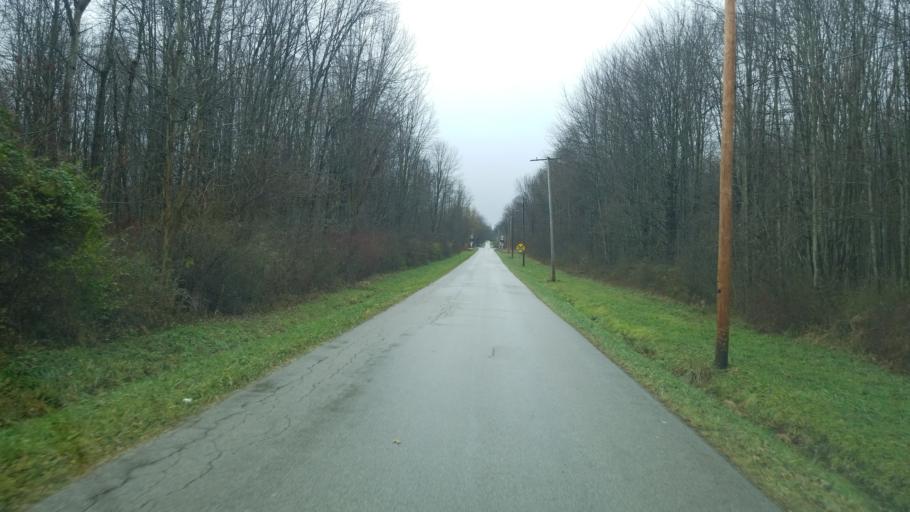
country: US
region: Ohio
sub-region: Ashtabula County
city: North Kingsville
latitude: 41.9015
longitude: -80.7233
